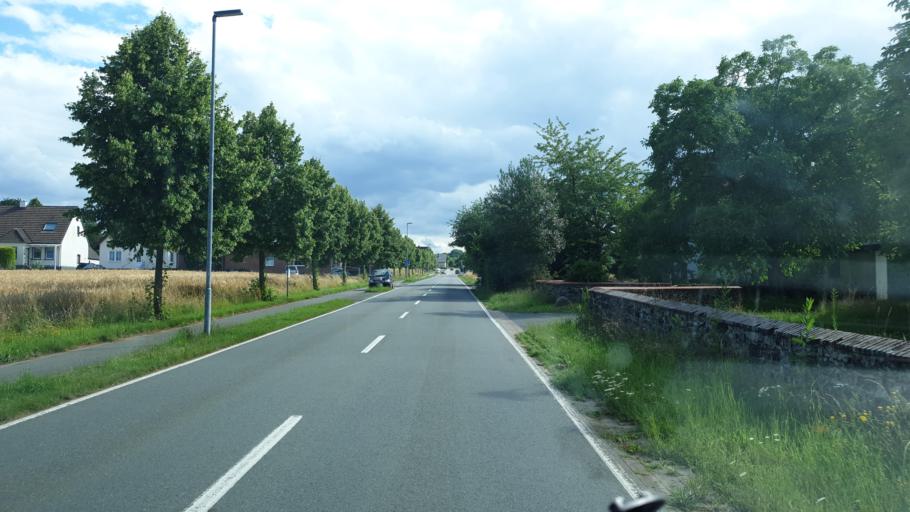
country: DE
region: North Rhine-Westphalia
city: Bad Oeynhausen
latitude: 52.1885
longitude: 8.7814
